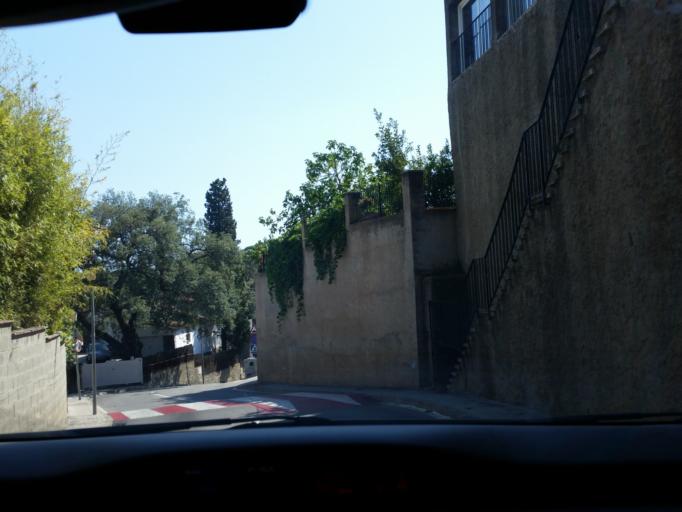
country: ES
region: Catalonia
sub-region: Provincia de Barcelona
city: Cabrils
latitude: 41.5283
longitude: 2.3657
